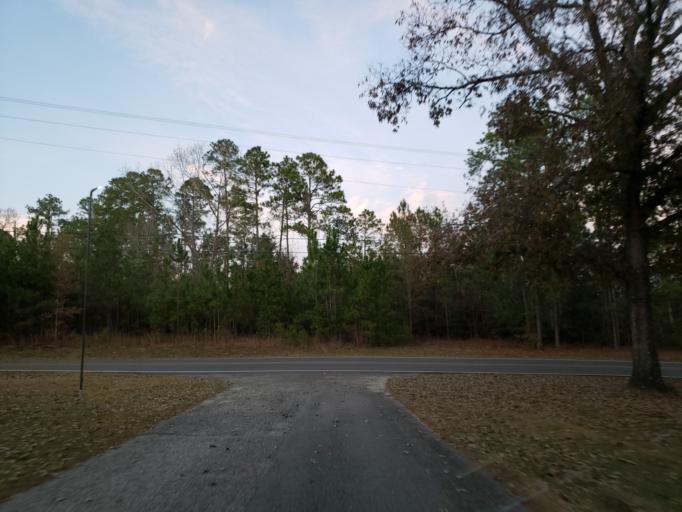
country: US
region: Mississippi
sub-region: Lamar County
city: West Hattiesburg
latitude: 31.2504
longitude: -89.3316
